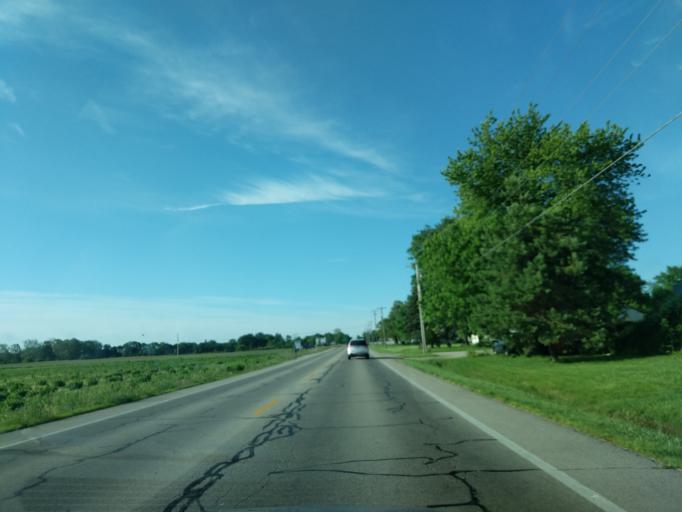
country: US
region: Indiana
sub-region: Madison County
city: Ingalls
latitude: 39.8882
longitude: -85.7705
